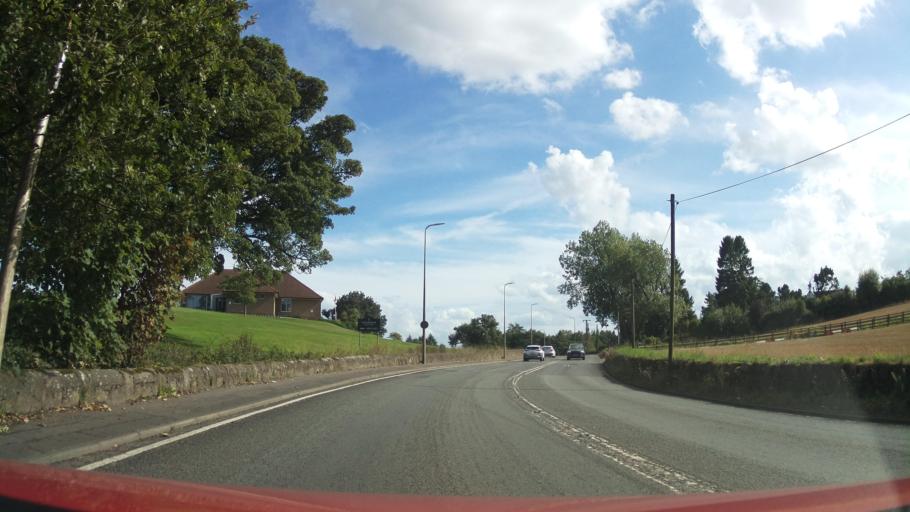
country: GB
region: Scotland
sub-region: Falkirk
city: Larbert
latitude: 56.0356
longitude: -3.8547
